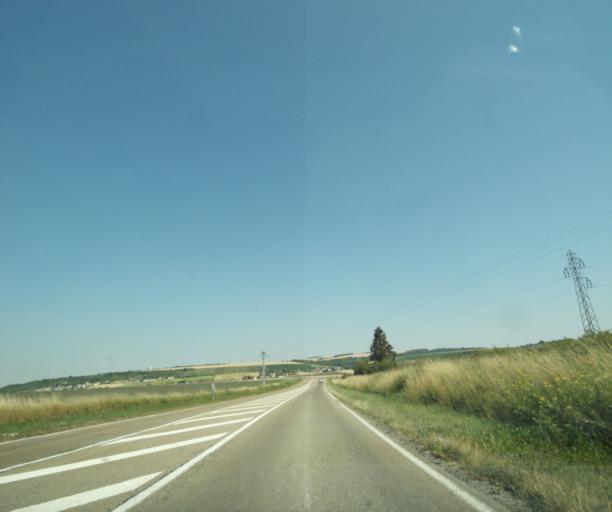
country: FR
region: Champagne-Ardenne
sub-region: Departement de la Marne
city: Vitry-le-Francois
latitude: 48.7513
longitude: 4.5911
